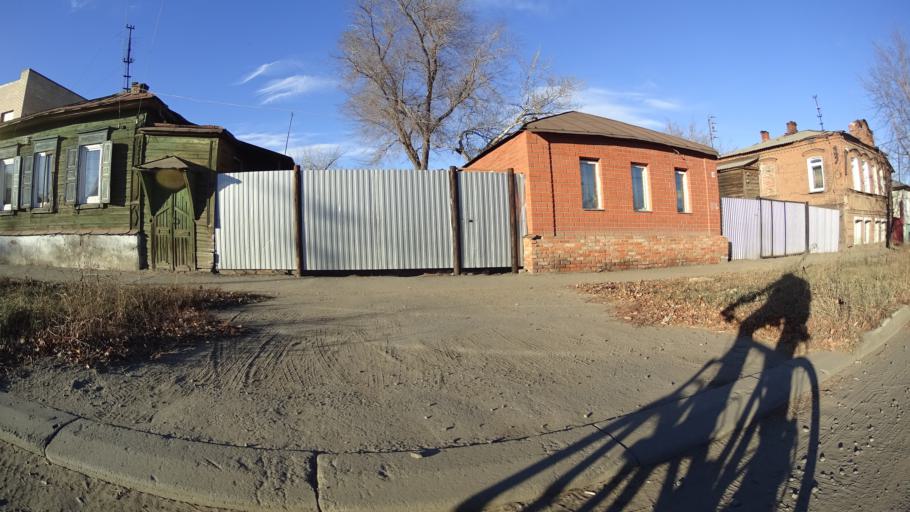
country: RU
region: Chelyabinsk
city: Troitsk
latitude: 54.0816
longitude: 61.5436
